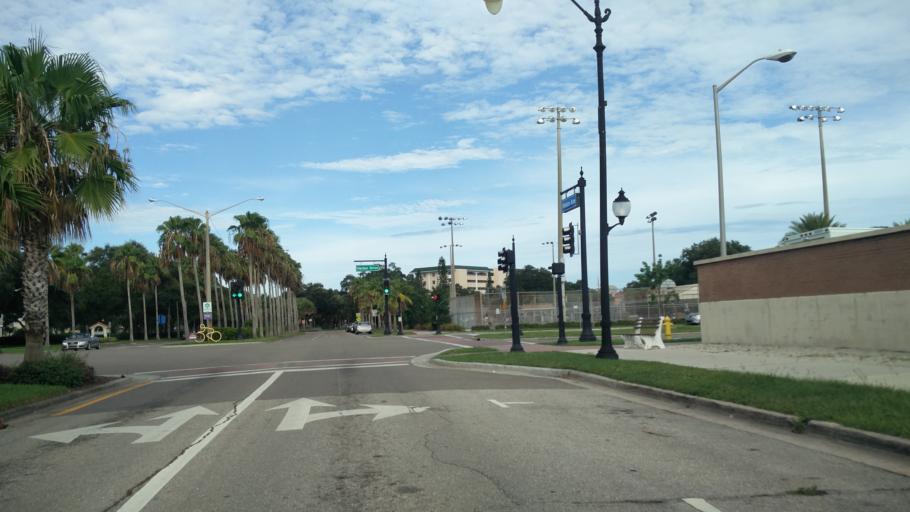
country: US
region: Florida
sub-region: Sarasota County
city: Venice
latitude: 27.1000
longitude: -82.4496
